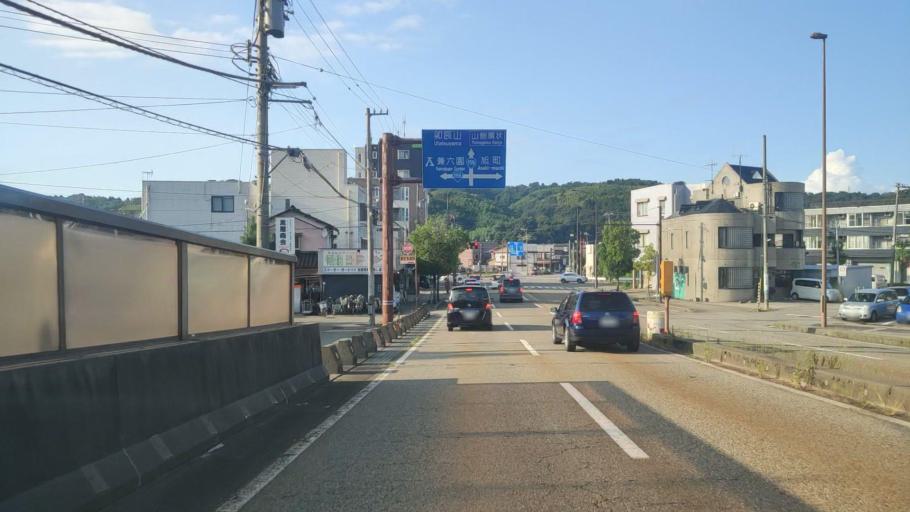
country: JP
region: Ishikawa
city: Kanazawa-shi
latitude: 36.5596
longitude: 136.6772
